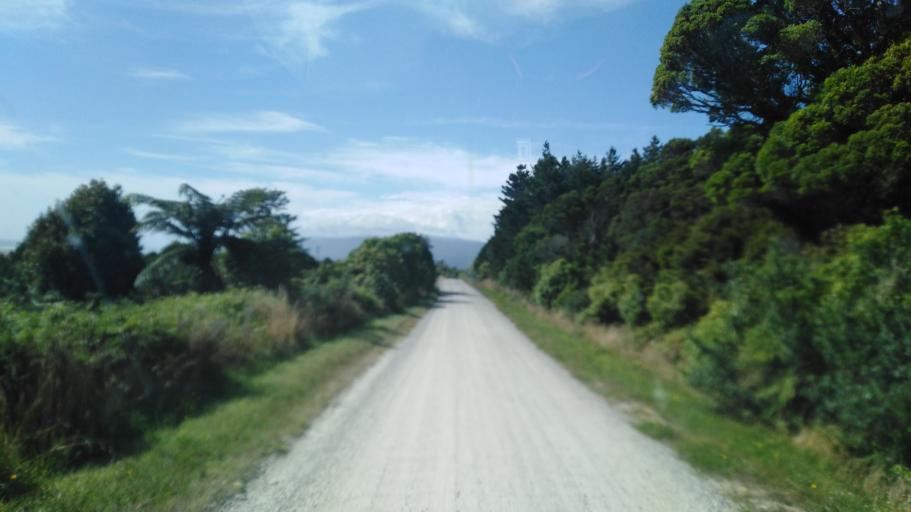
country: NZ
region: West Coast
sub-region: Buller District
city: Westport
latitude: -41.2652
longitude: 172.1135
